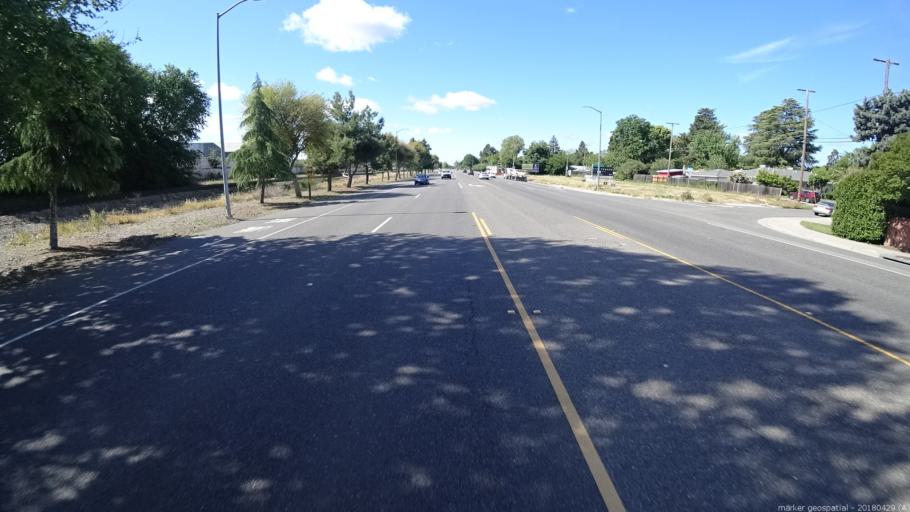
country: US
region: California
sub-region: Yolo County
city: West Sacramento
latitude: 38.5660
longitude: -121.5262
